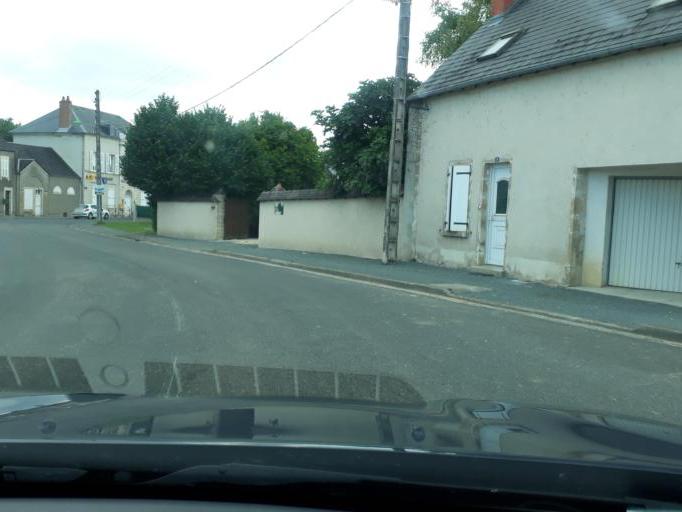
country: FR
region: Centre
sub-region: Departement du Cher
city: Baugy
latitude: 47.0815
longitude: 2.7302
